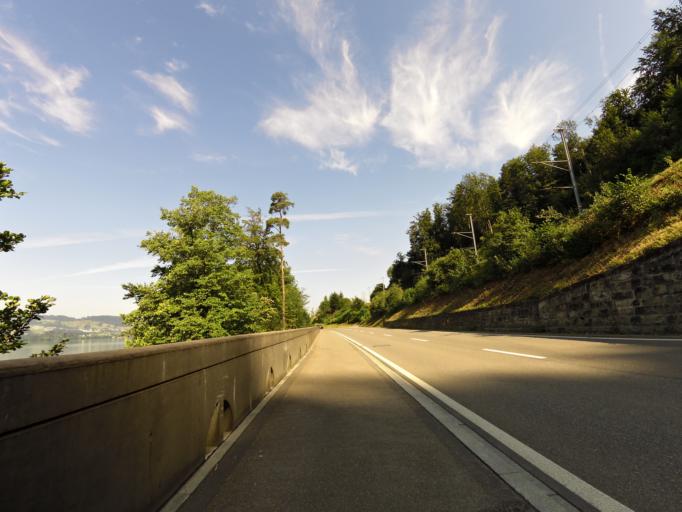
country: CH
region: Zug
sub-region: Zug
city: Walchwil
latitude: 47.1170
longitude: 8.4992
